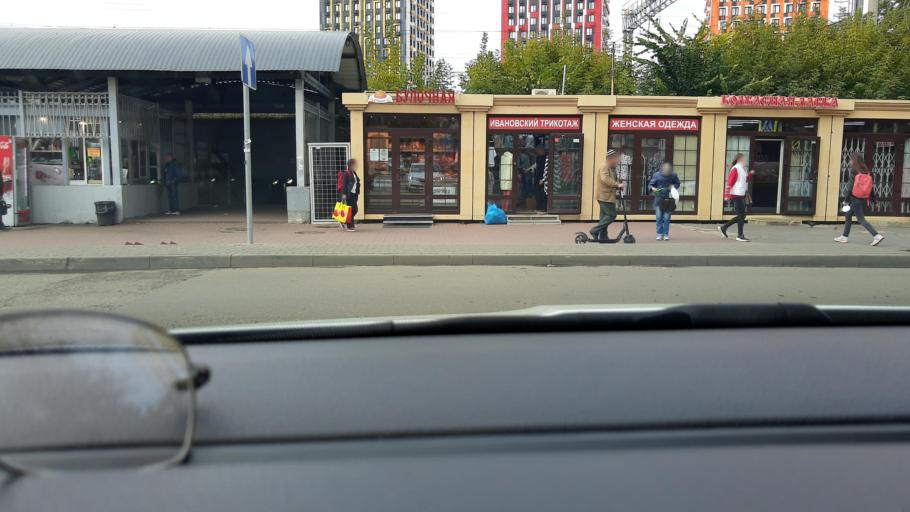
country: RU
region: Moskovskaya
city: Pavshino
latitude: 55.8148
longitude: 37.3425
